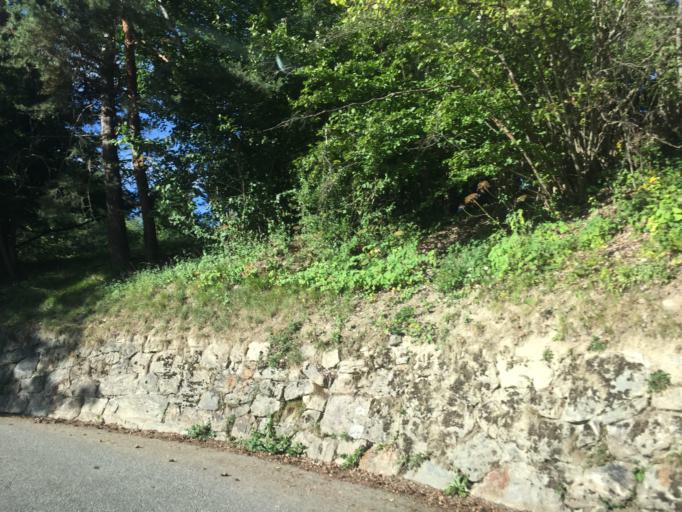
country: FR
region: Rhone-Alpes
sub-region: Departement de la Savoie
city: Moutiers
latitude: 45.5067
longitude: 6.5855
